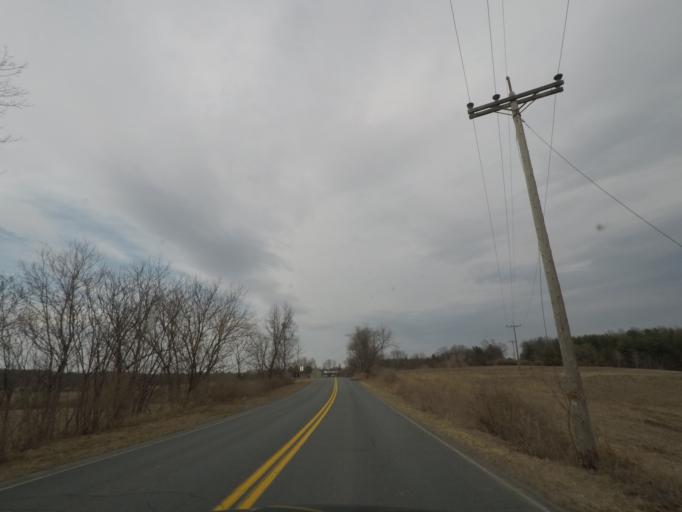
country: US
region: New York
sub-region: Washington County
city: Cambridge
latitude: 42.9400
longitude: -73.4907
